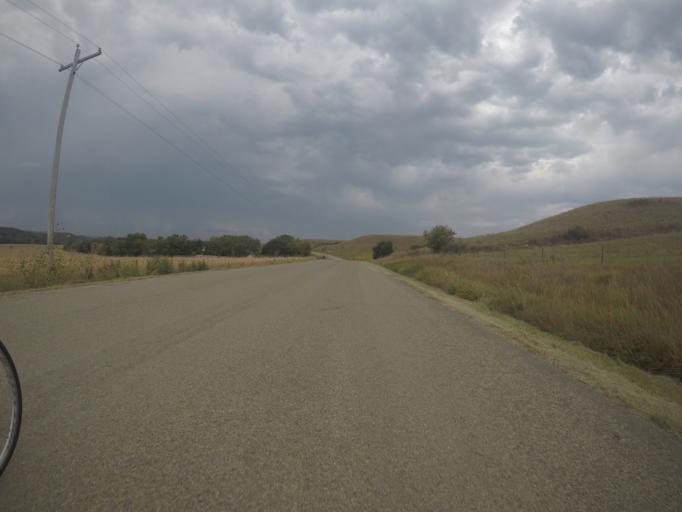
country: US
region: Kansas
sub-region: Riley County
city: Ogden
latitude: 38.9692
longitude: -96.6322
